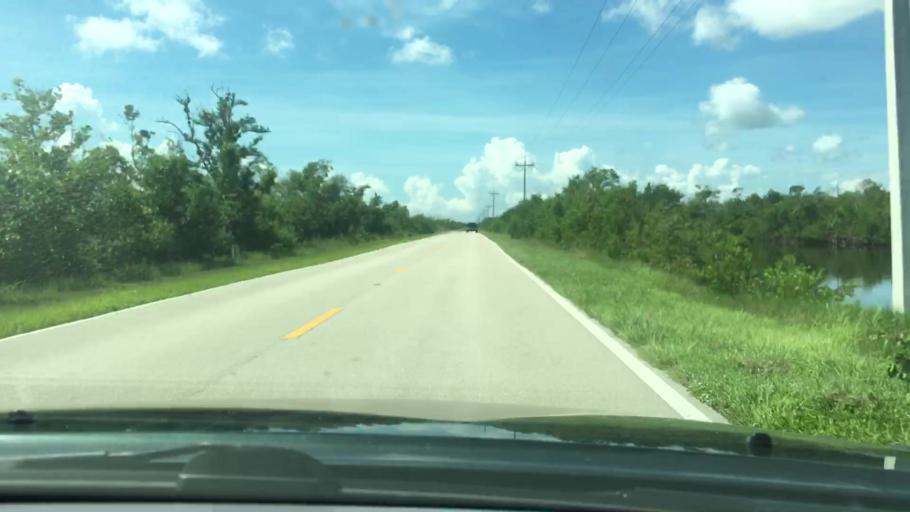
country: US
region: Florida
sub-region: Collier County
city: Marco
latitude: 25.9497
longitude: -81.6420
